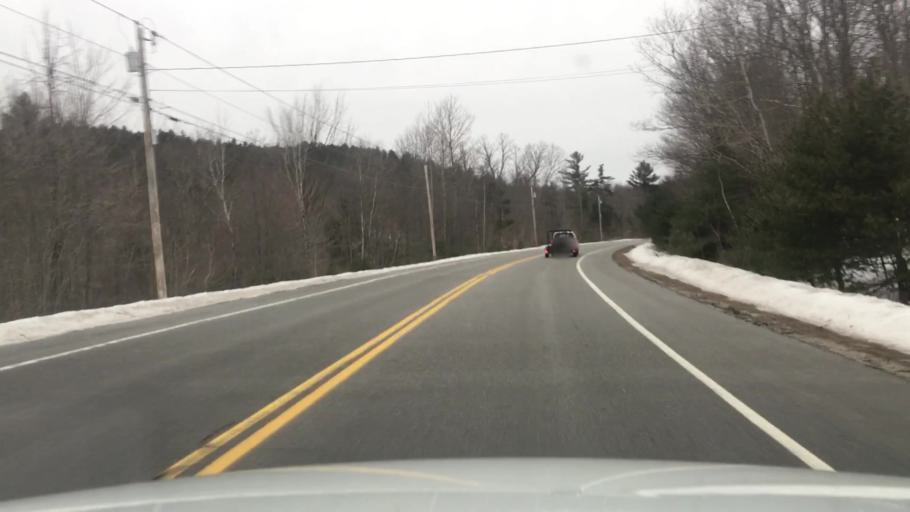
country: US
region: Maine
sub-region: York County
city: Limerick
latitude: 43.7365
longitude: -70.8169
